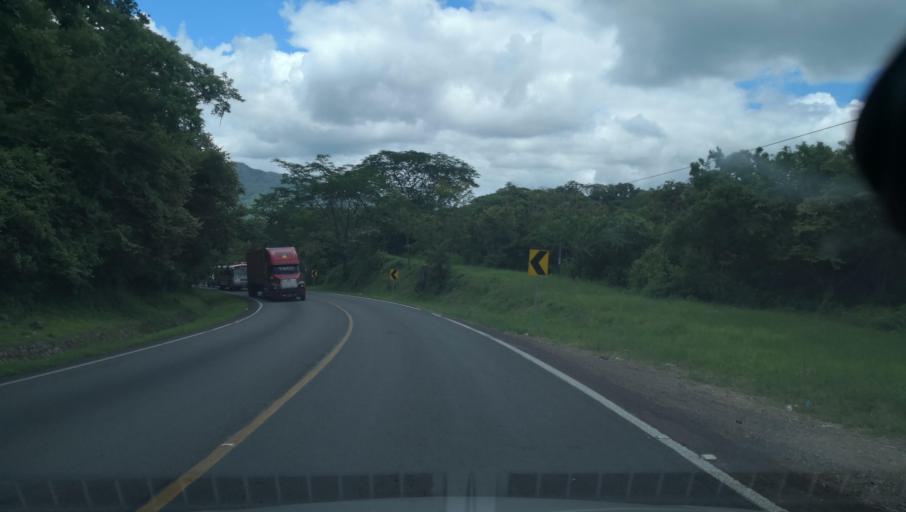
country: NI
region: Esteli
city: Condega
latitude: 13.2499
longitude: -86.3607
